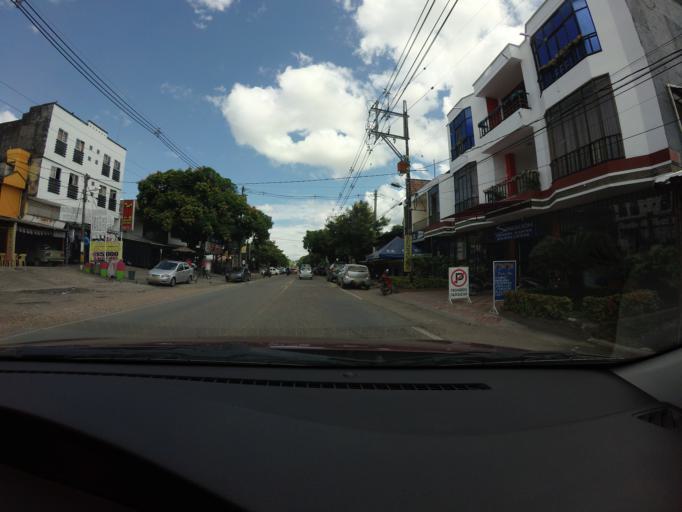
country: CO
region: Antioquia
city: Puerto Triunfo
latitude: 5.8984
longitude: -74.7357
